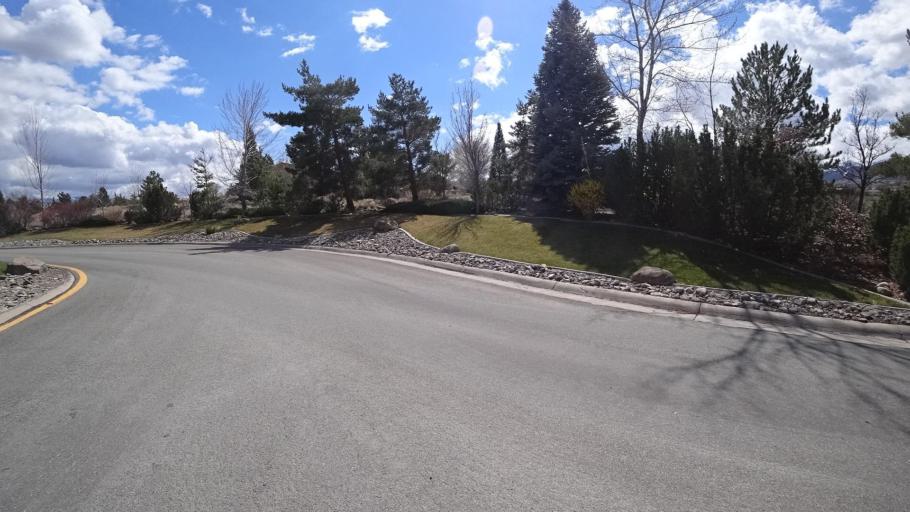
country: US
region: Nevada
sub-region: Washoe County
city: Reno
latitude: 39.4191
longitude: -119.7910
